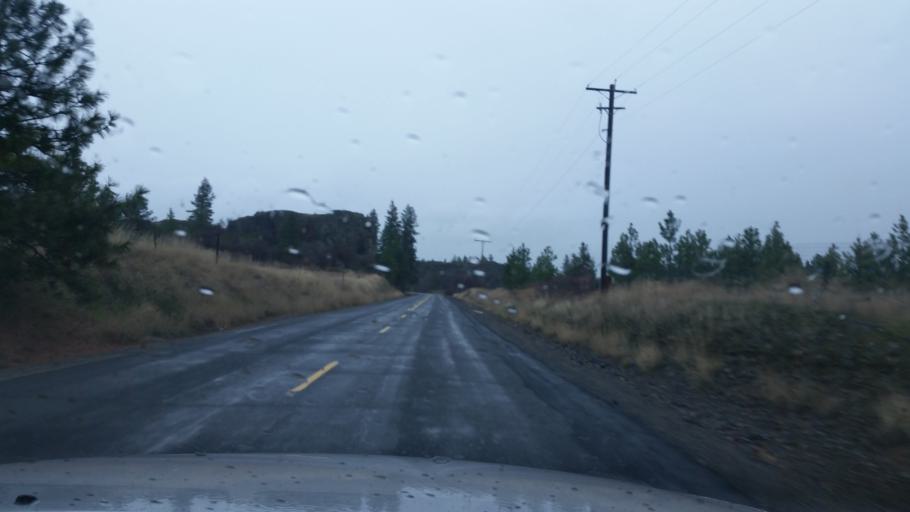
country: US
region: Washington
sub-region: Spokane County
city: Airway Heights
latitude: 47.6943
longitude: -117.5719
